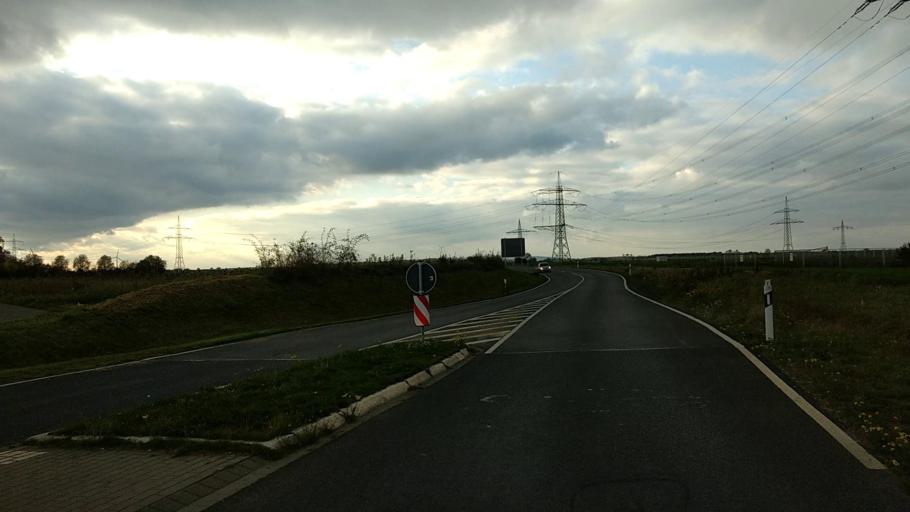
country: DE
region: North Rhine-Westphalia
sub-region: Regierungsbezirk Koln
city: Kerpen
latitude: 50.8647
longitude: 6.6539
